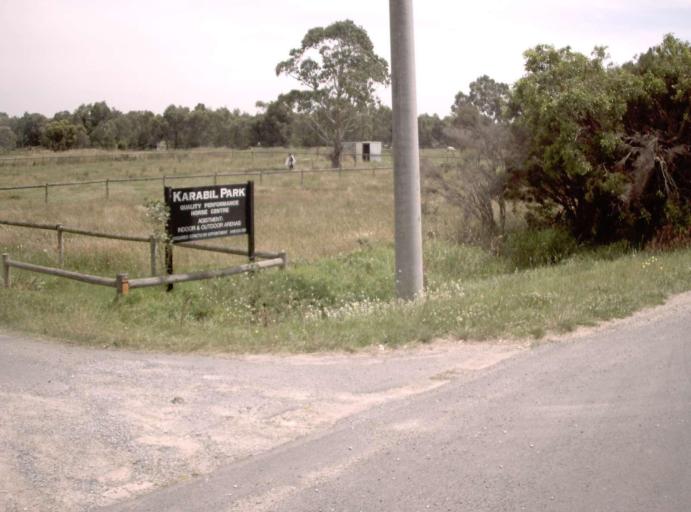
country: AU
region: Victoria
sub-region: Frankston
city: Skye
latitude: -38.1151
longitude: 145.2318
